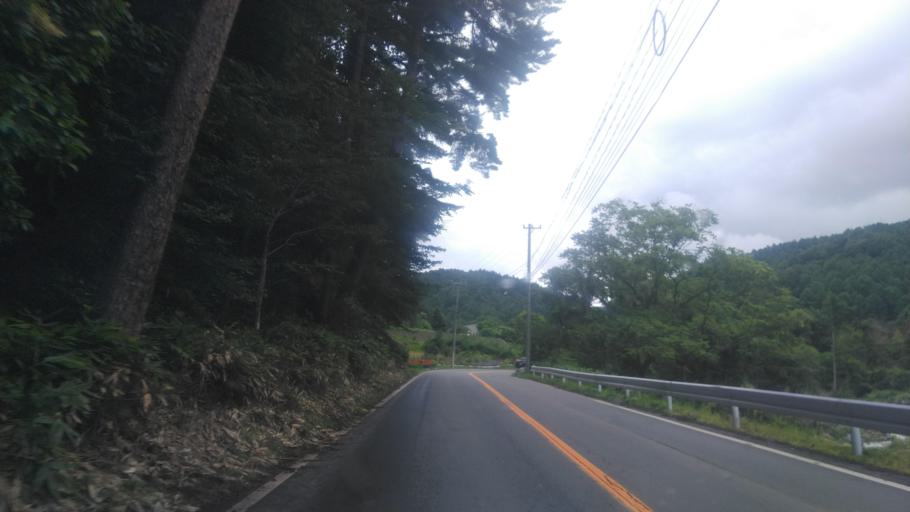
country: JP
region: Nagano
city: Ueda
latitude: 36.4895
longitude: 138.3711
